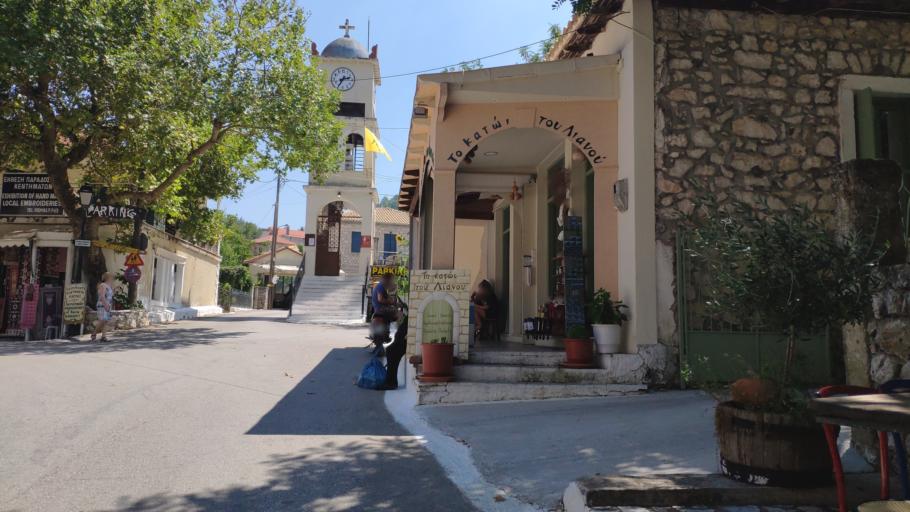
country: GR
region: Ionian Islands
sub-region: Lefkada
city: Nidri
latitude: 38.7591
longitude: 20.6489
